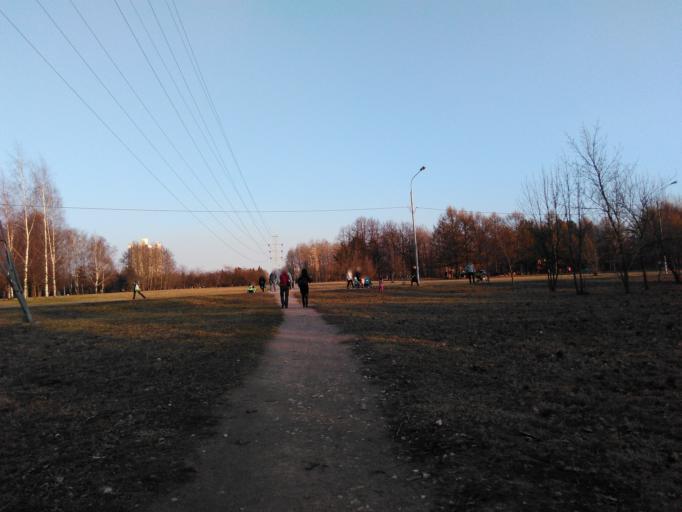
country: RU
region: Moscow
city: Nikol'skoye
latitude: 55.6848
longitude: 37.4980
